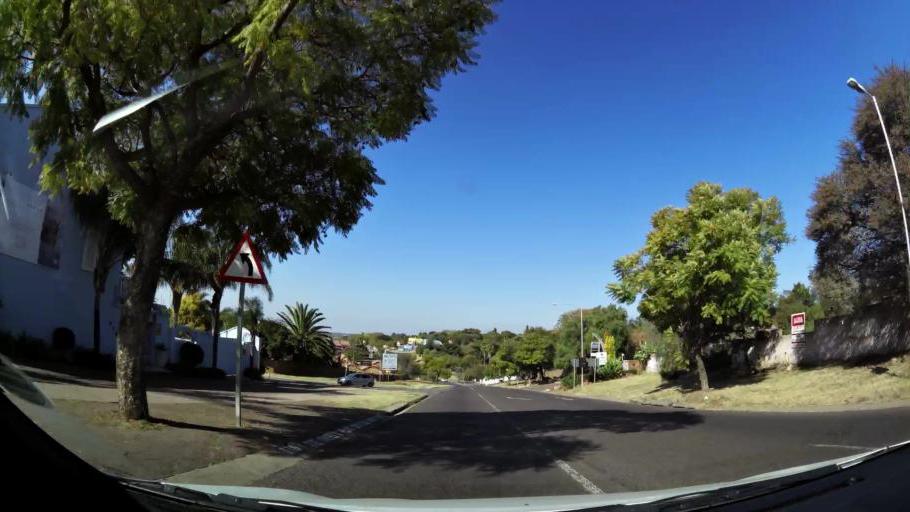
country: ZA
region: Gauteng
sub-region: City of Tshwane Metropolitan Municipality
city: Centurion
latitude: -25.8189
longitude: 28.2846
